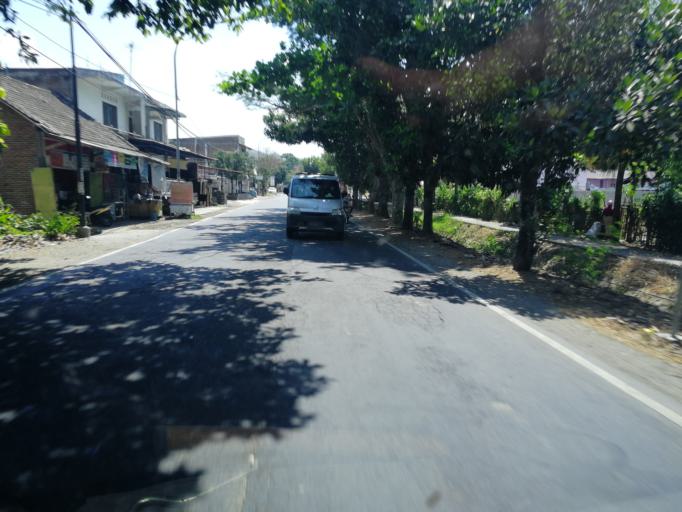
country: ID
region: West Nusa Tenggara
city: Jelateng Timur
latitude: -8.7005
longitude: 116.1011
